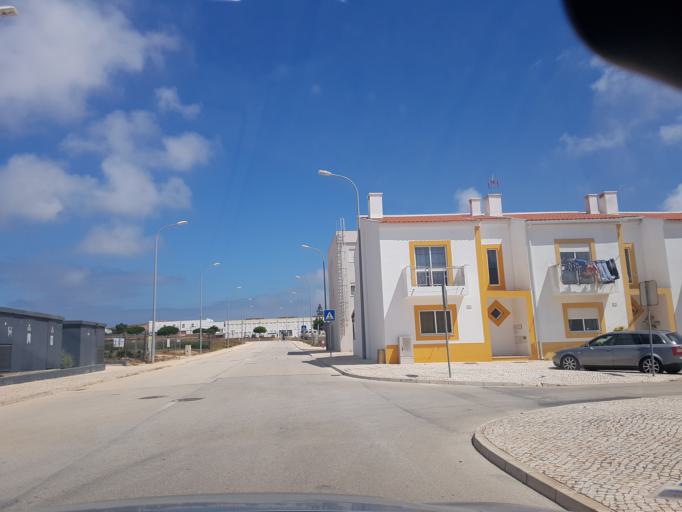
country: PT
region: Faro
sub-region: Vila do Bispo
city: Vila do Bispo
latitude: 37.0799
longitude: -8.9136
